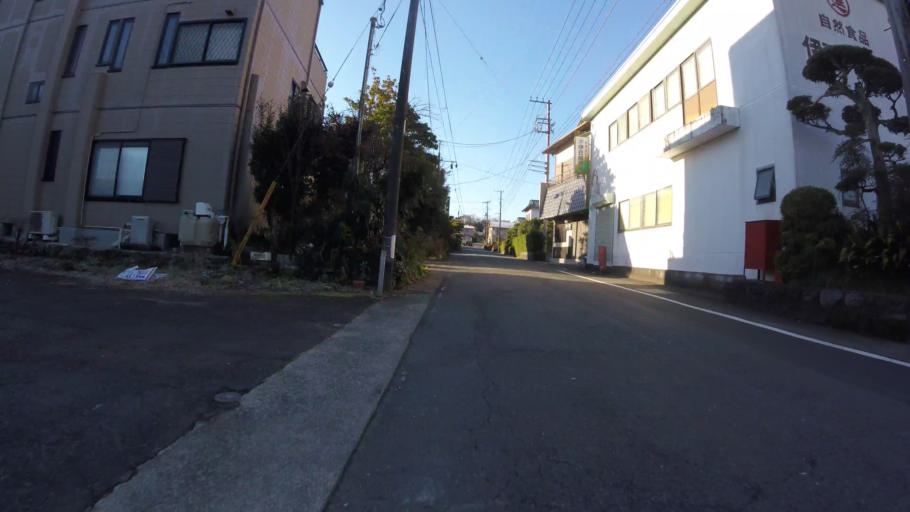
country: JP
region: Shizuoka
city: Ito
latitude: 34.9664
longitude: 138.9422
